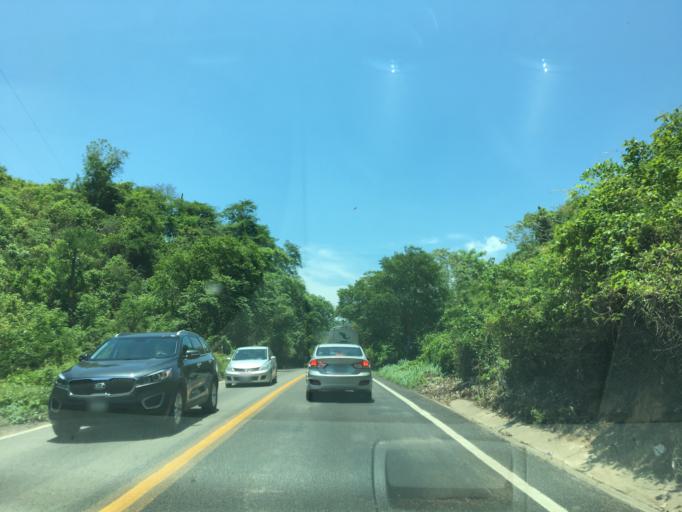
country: MX
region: Nayarit
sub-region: Bahia de Banderas
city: Corral del Risco (Punta de Mita)
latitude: 20.8528
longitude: -105.4246
